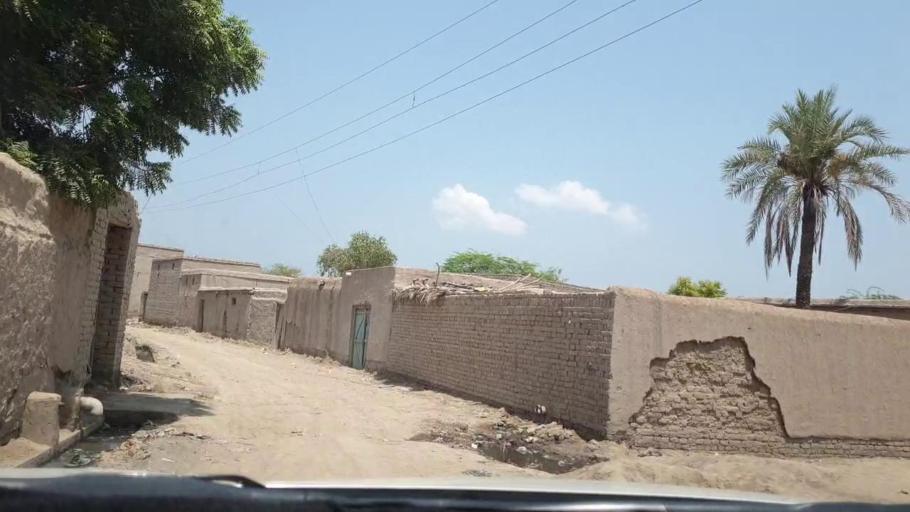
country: PK
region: Sindh
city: Radhan
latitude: 27.2415
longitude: 68.0057
